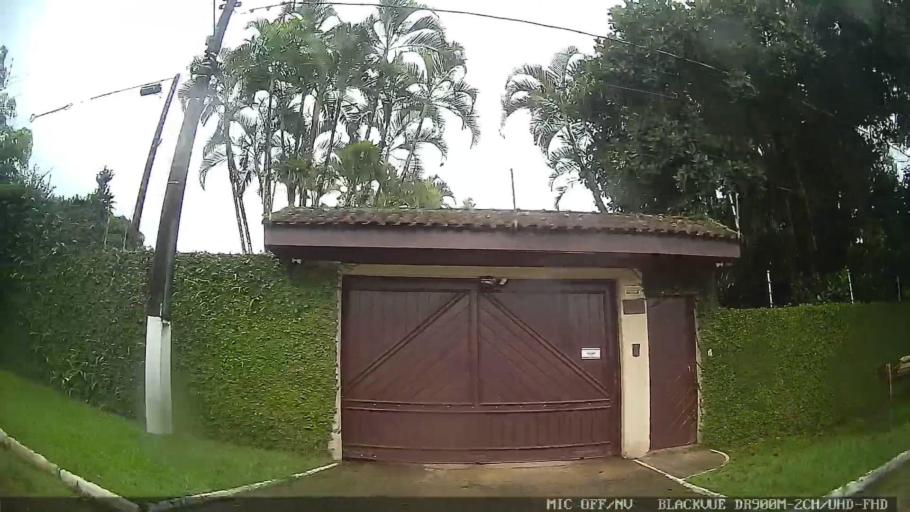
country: BR
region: Sao Paulo
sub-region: Itanhaem
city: Itanhaem
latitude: -24.1749
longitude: -46.8278
